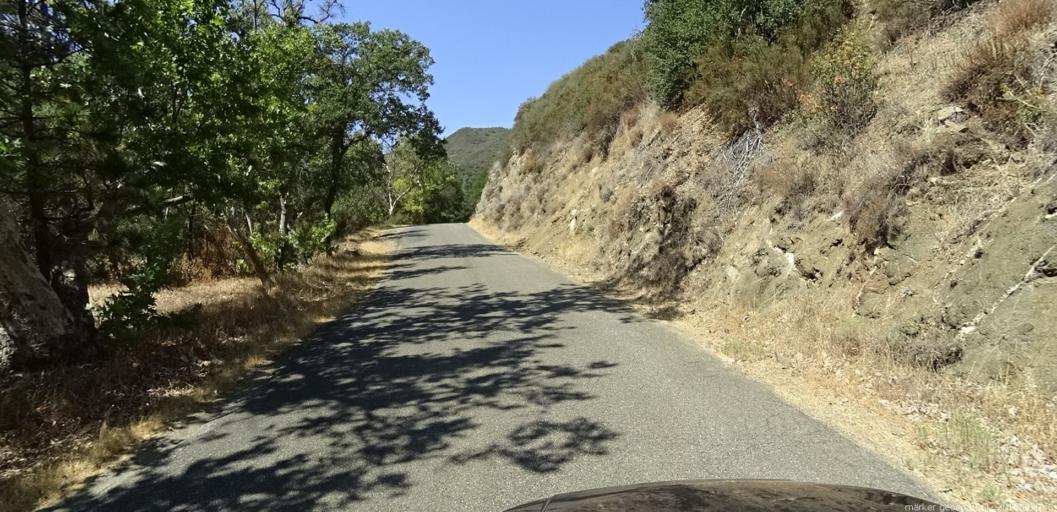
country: US
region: California
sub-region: Monterey County
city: King City
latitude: 35.9974
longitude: -121.3795
